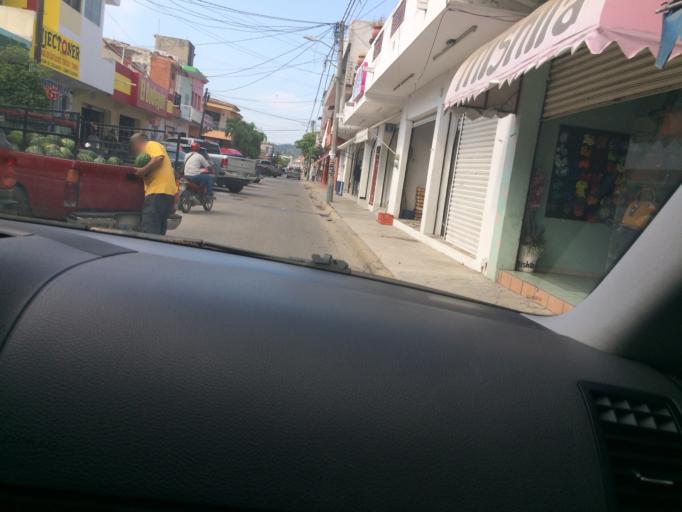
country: MX
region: Jalisco
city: Cihuatlan
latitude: 19.2378
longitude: -104.5581
